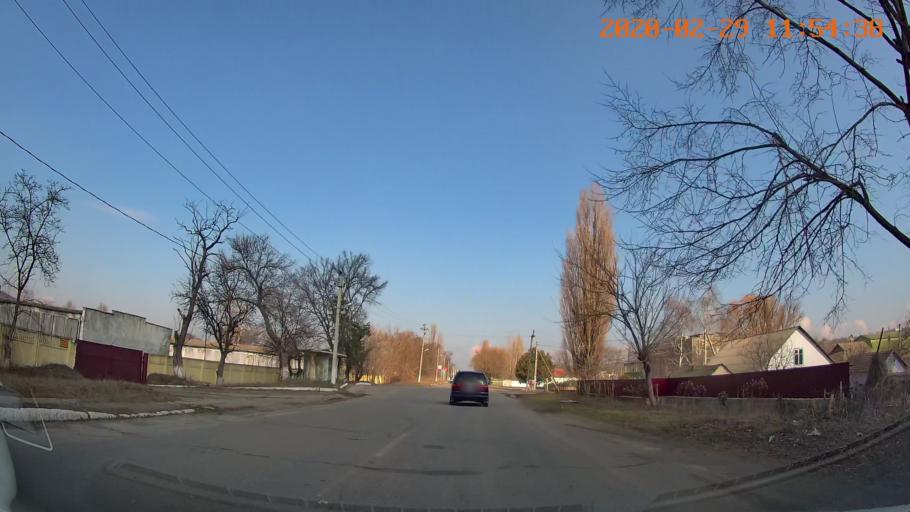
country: MD
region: Telenesti
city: Ribnita
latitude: 47.7855
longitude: 28.9957
